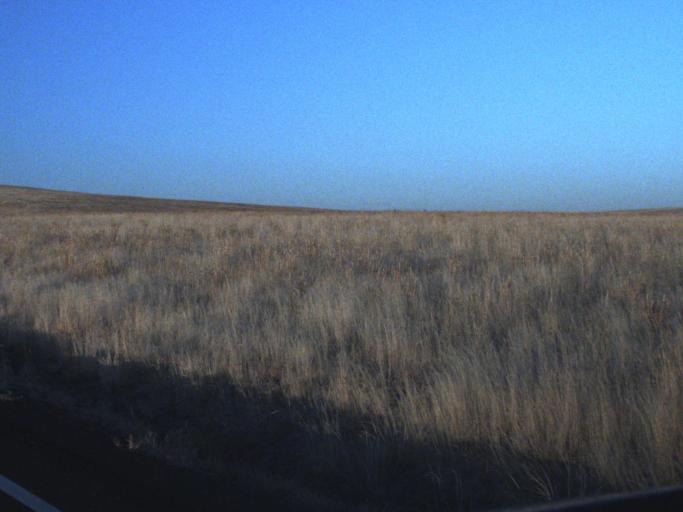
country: US
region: Washington
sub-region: Adams County
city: Ritzville
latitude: 46.9759
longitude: -118.6638
